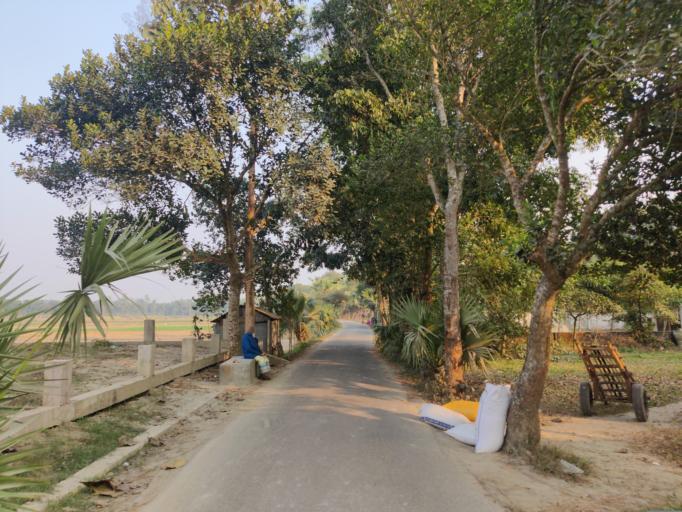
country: BD
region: Dhaka
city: Narsingdi
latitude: 24.0950
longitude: 90.7078
